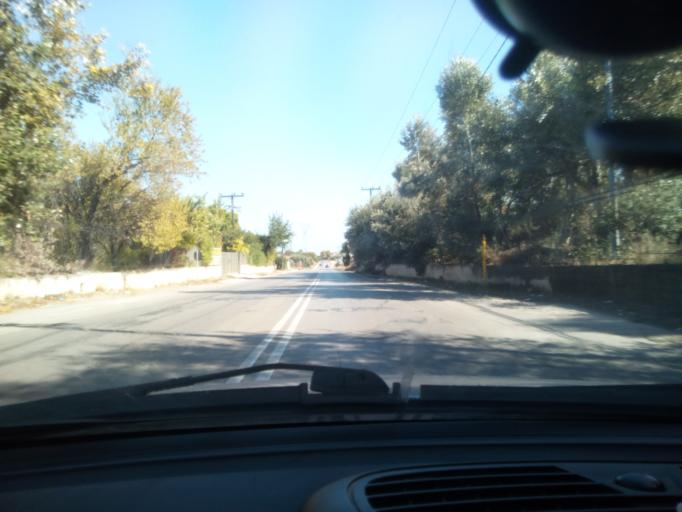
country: GR
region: Central Greece
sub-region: Nomos Evvoias
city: Vasilikon
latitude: 38.4200
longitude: 23.6826
